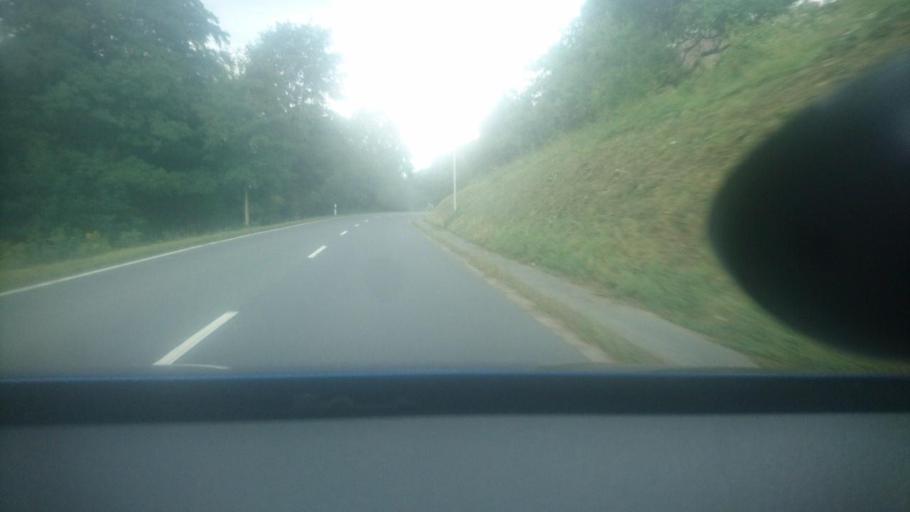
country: DE
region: Hesse
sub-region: Regierungsbezirk Darmstadt
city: Frankisch-Crumbach
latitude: 49.7386
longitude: 8.8892
